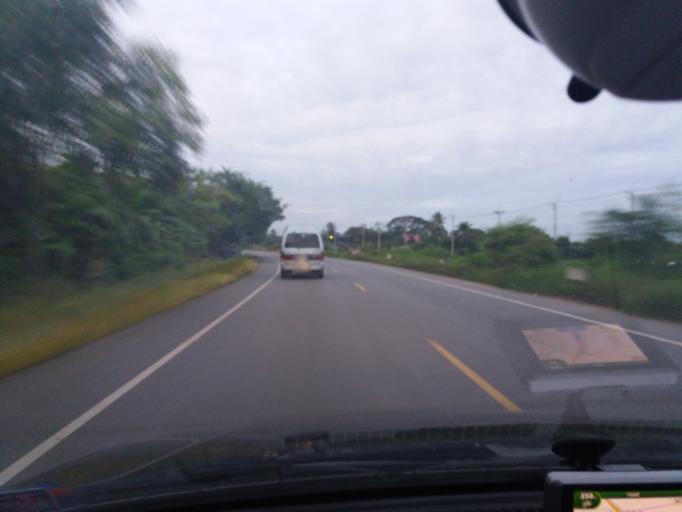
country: TH
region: Suphan Buri
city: Ban Sam Chuk
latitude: 14.7391
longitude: 100.0924
